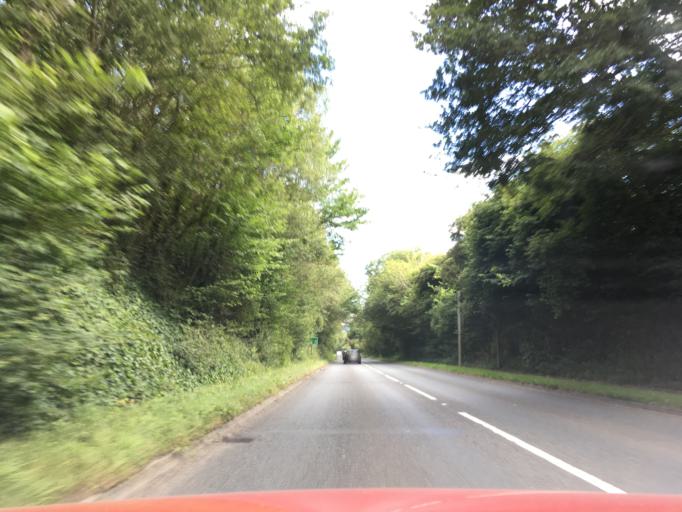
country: GB
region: England
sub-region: Somerset
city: Yeovil
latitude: 50.9213
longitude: -2.6342
